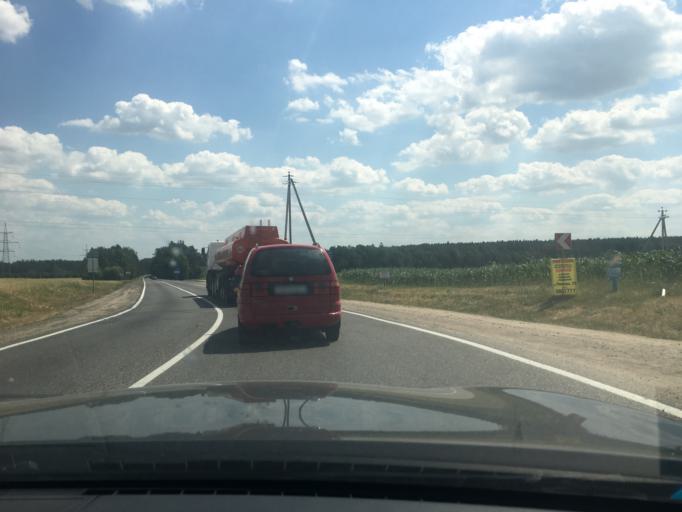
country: BY
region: Grodnenskaya
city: Hrodna
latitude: 53.6181
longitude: 23.8722
